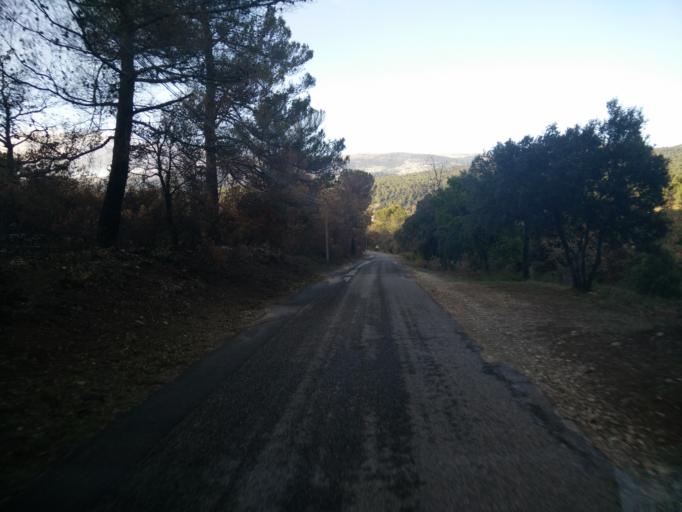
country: FR
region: Provence-Alpes-Cote d'Azur
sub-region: Departement du Var
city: Signes
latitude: 43.2781
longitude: 5.8454
